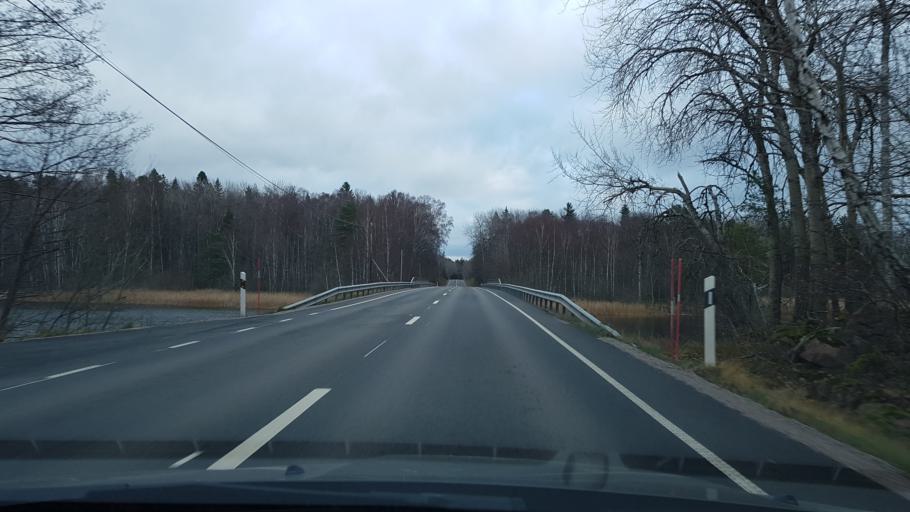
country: SE
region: Stockholm
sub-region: Norrtalje Kommun
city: Skanninge
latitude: 60.0133
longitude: 18.3418
